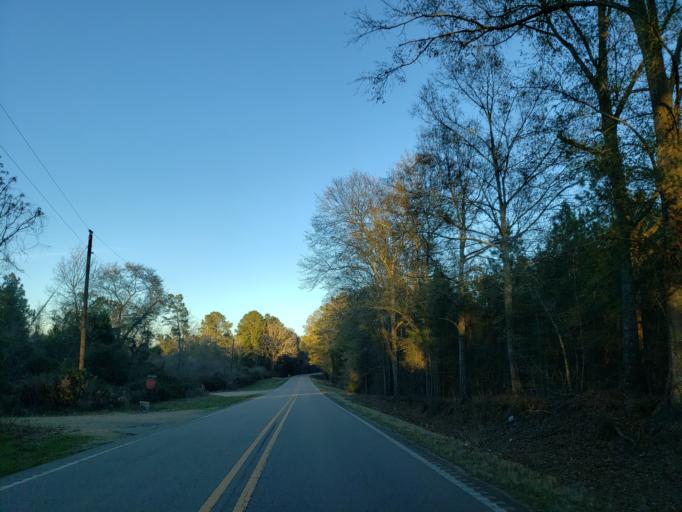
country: US
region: Mississippi
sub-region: Covington County
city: Collins
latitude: 31.5610
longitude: -89.4428
